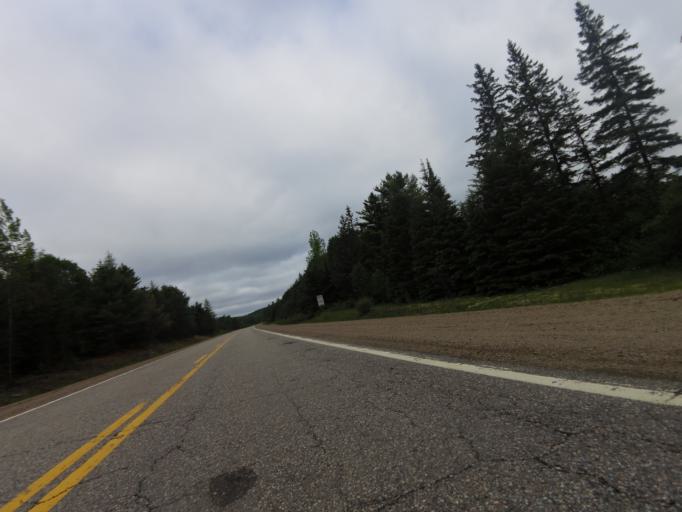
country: CA
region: Quebec
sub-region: Outaouais
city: Shawville
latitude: 45.9069
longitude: -76.2997
